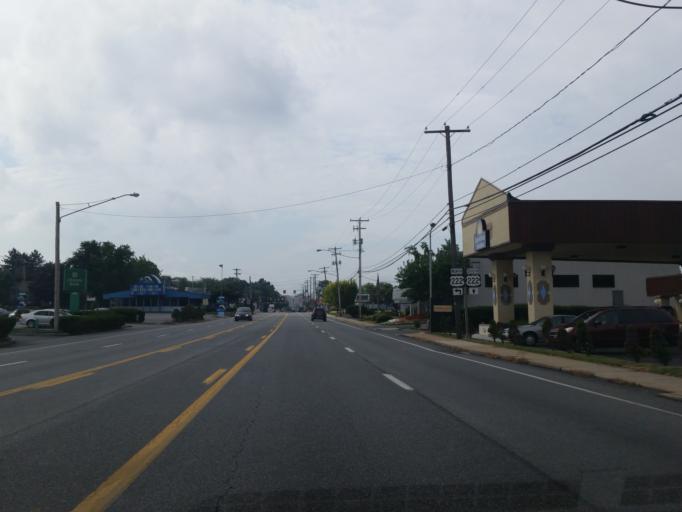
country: US
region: Pennsylvania
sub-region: Lancaster County
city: Lancaster
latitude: 40.0635
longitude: -76.3067
